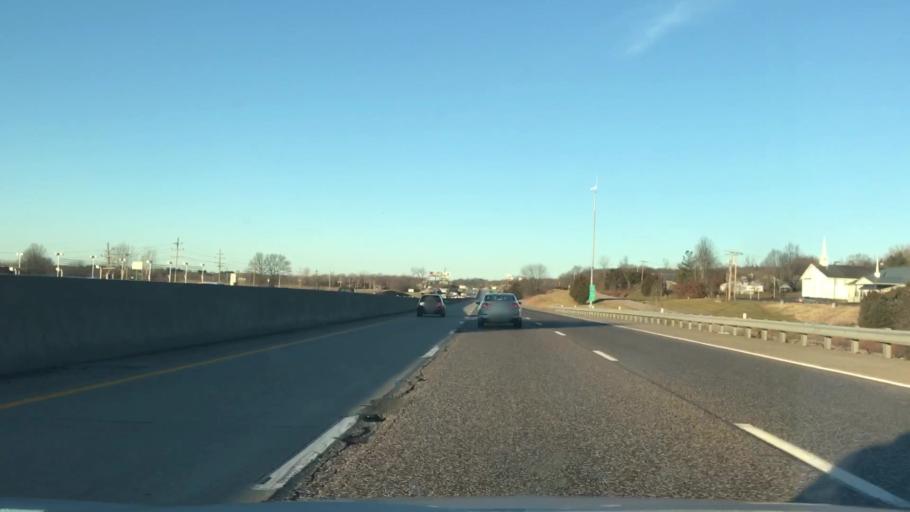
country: US
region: Missouri
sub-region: Franklin County
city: Pacific
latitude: 38.4877
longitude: -90.7764
